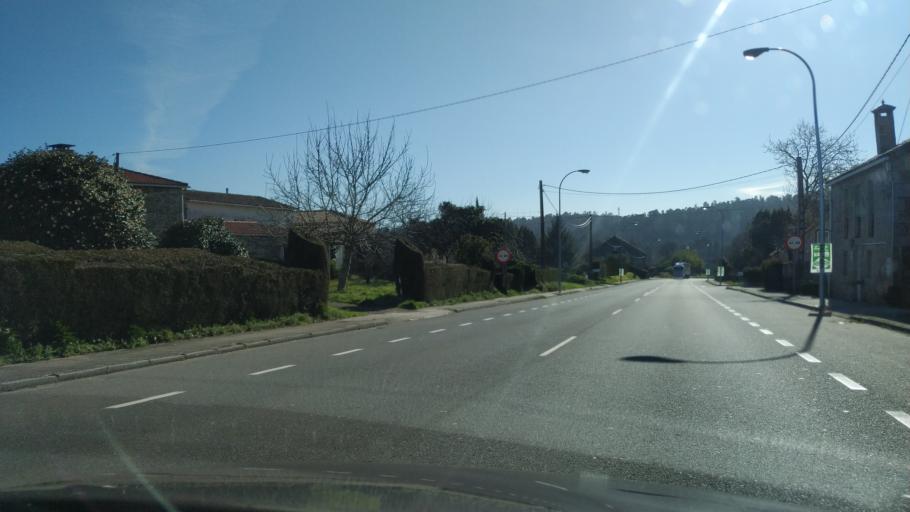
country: ES
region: Galicia
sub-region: Provincia de Pontevedra
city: Silleda
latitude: 42.7358
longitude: -8.3228
